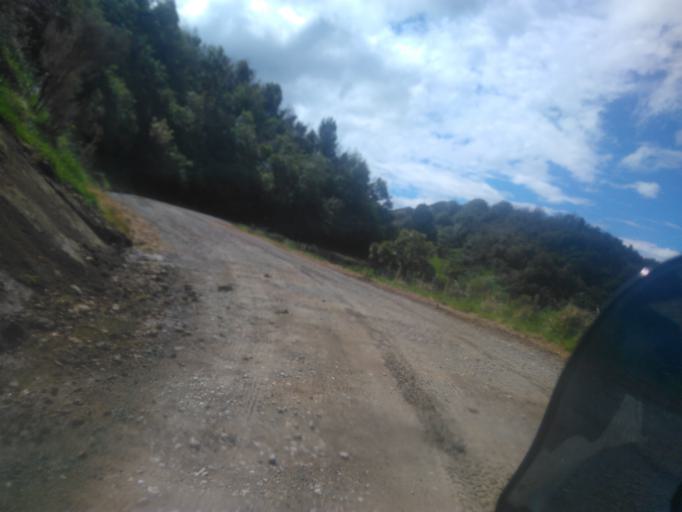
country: NZ
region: Hawke's Bay
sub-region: Wairoa District
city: Wairoa
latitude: -38.7786
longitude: 177.6224
